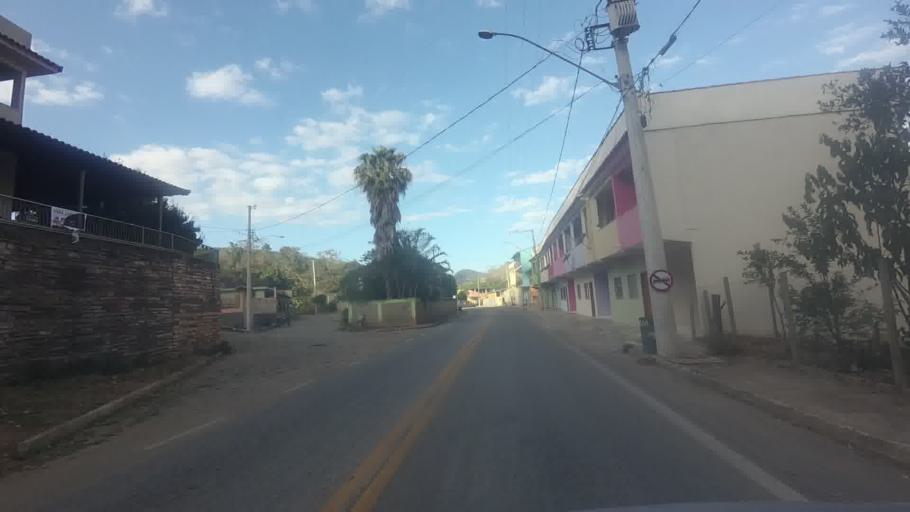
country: BR
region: Espirito Santo
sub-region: Mimoso Do Sul
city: Mimoso do Sul
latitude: -20.9437
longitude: -41.3348
